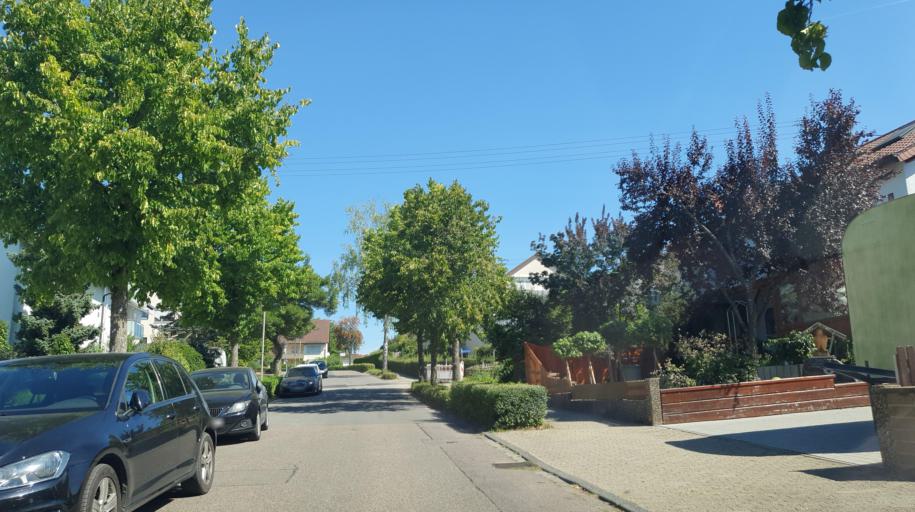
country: DE
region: Baden-Wuerttemberg
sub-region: Regierungsbezirk Stuttgart
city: Bad Rappenau
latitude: 49.2401
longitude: 9.0949
